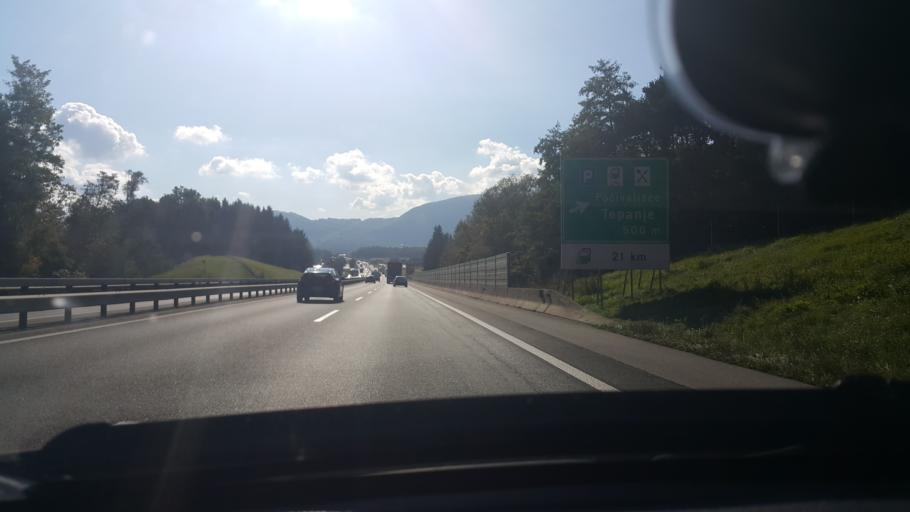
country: SI
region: Oplotnica
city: Oplotnica
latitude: 46.3545
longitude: 15.4963
